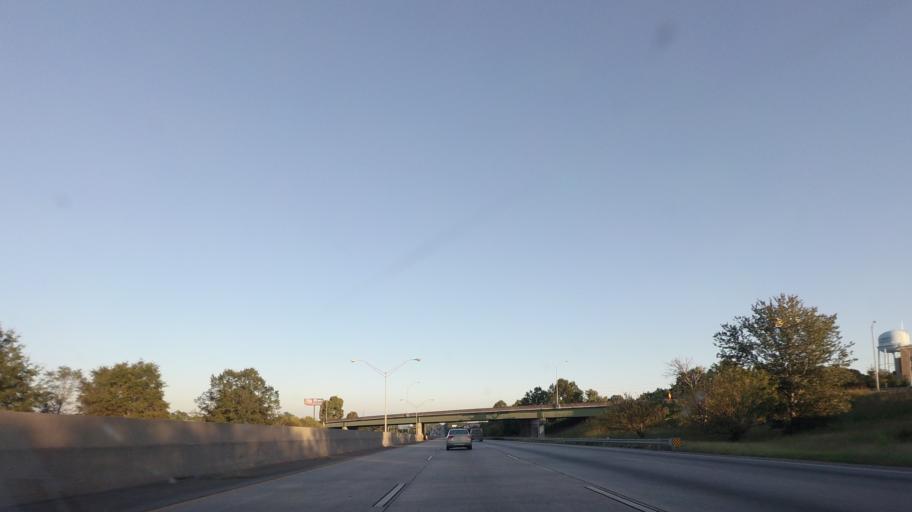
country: US
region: Georgia
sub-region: Monroe County
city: Forsyth
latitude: 33.0287
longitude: -83.9113
